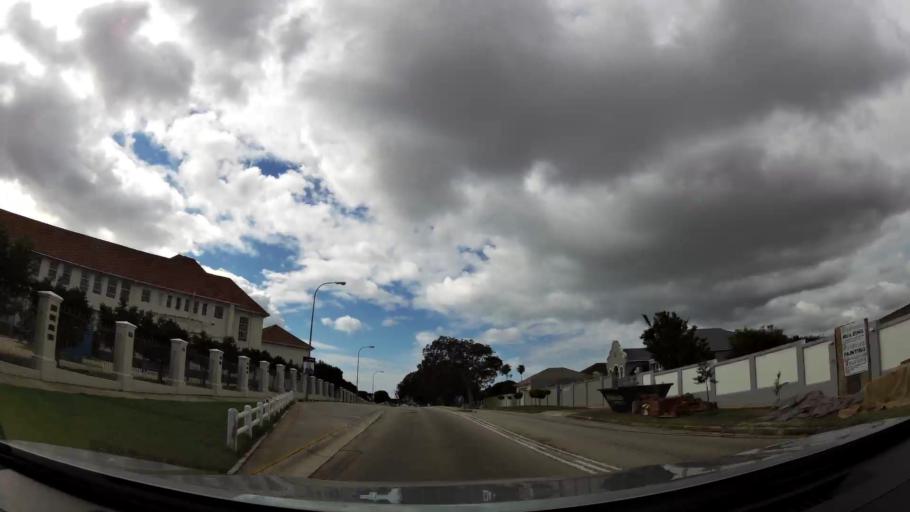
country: ZA
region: Eastern Cape
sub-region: Nelson Mandela Bay Metropolitan Municipality
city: Port Elizabeth
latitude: -33.9624
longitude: 25.5967
